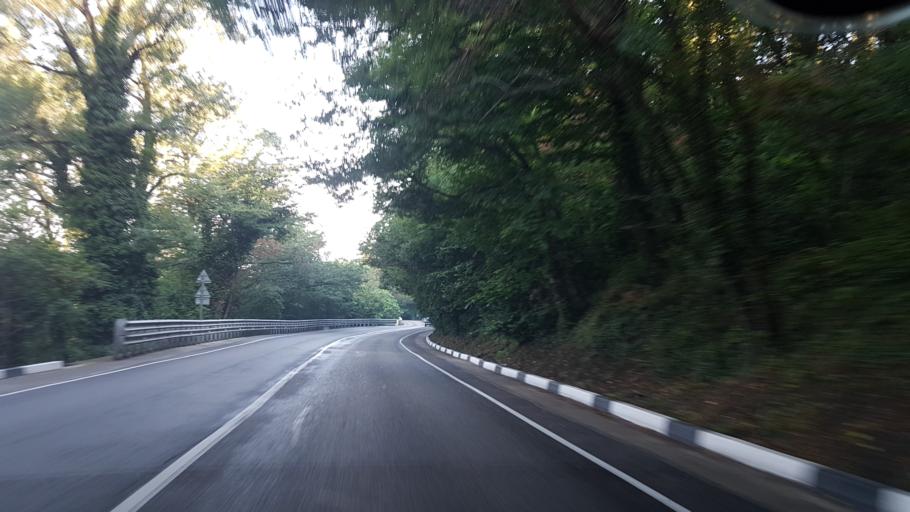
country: RU
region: Krasnodarskiy
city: Gornoye Loo
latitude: 43.6752
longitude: 39.6151
